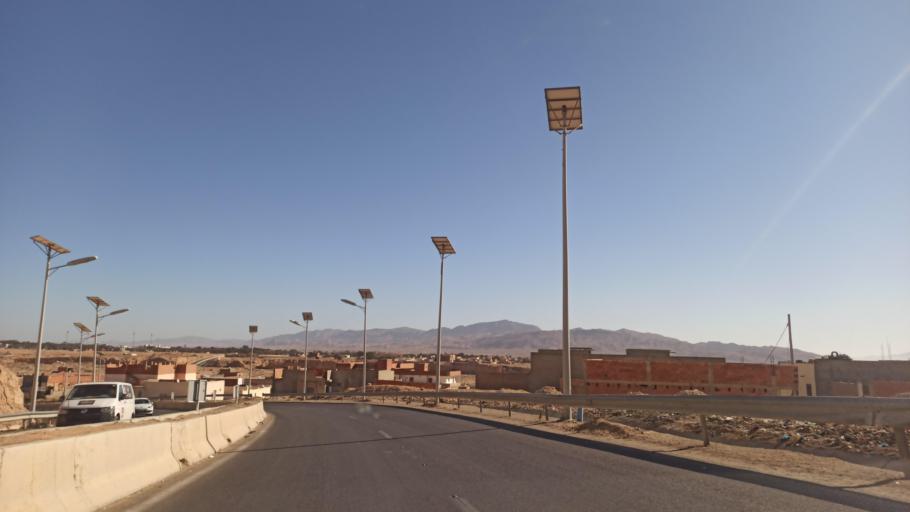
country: TN
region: Gafsa
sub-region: Gafsa Municipality
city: Gafsa
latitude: 34.4332
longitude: 8.7976
